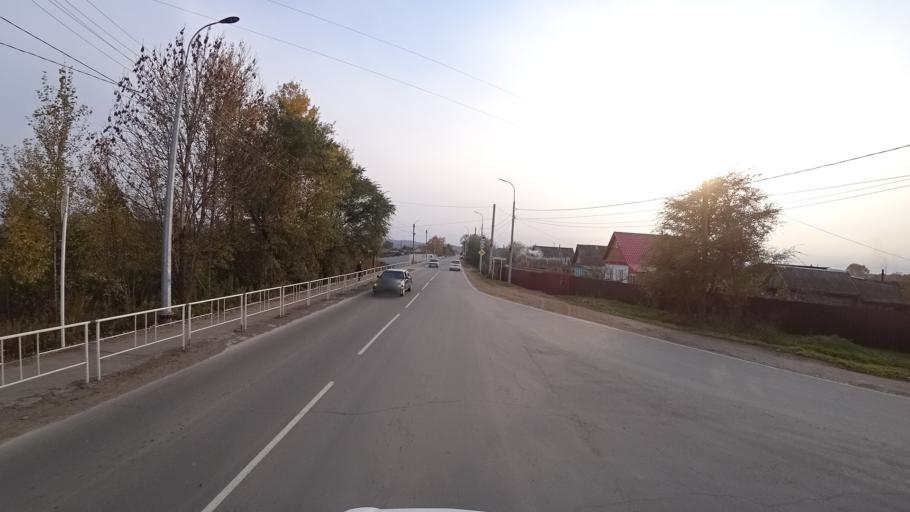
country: RU
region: Khabarovsk Krai
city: Amursk
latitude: 50.0923
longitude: 136.5037
